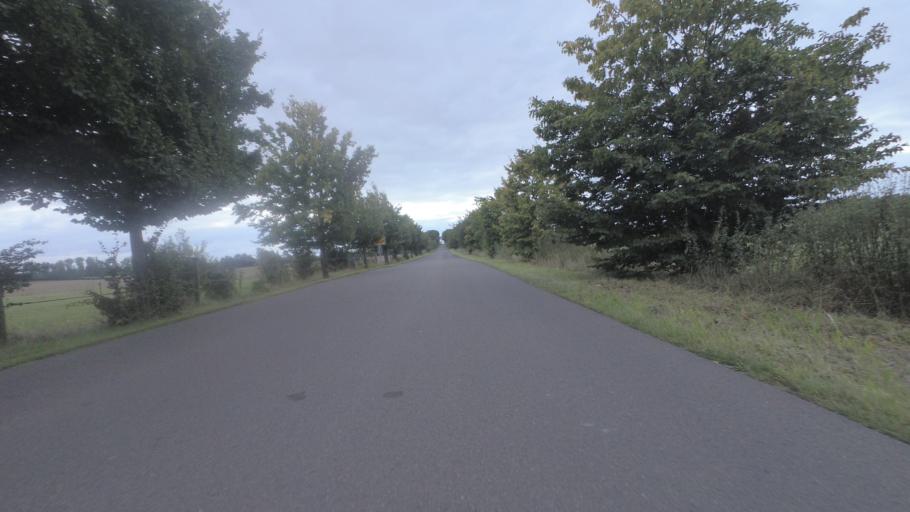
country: DE
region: Brandenburg
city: Neuenhagen
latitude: 52.5664
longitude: 13.6589
